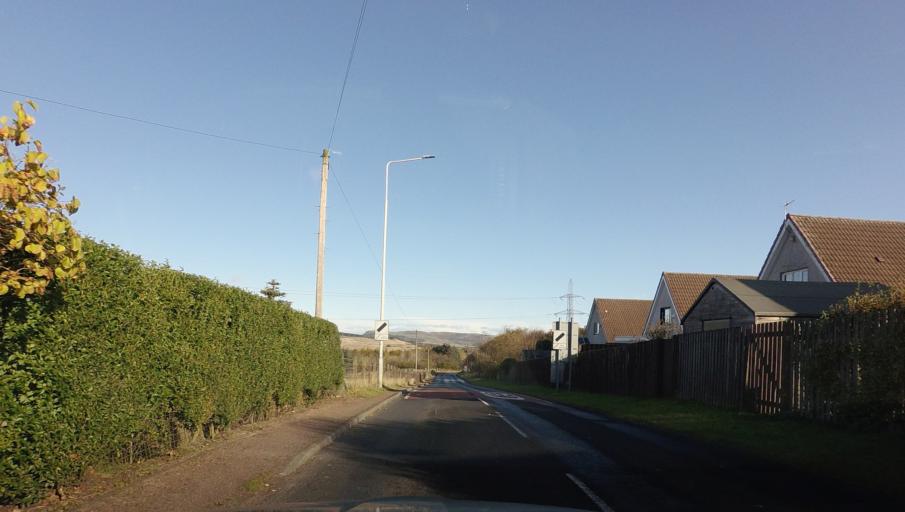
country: GB
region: Scotland
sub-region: Fife
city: Townhill
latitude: 56.1004
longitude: -3.4064
